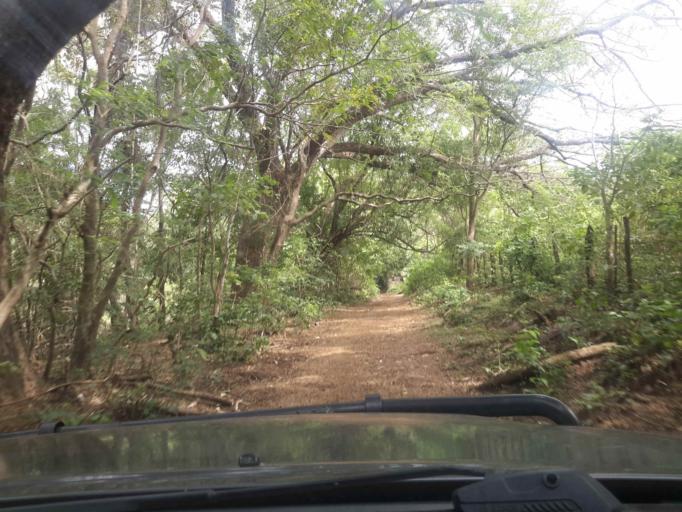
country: NI
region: Carazo
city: Santa Teresa
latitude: 11.6933
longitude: -86.2971
